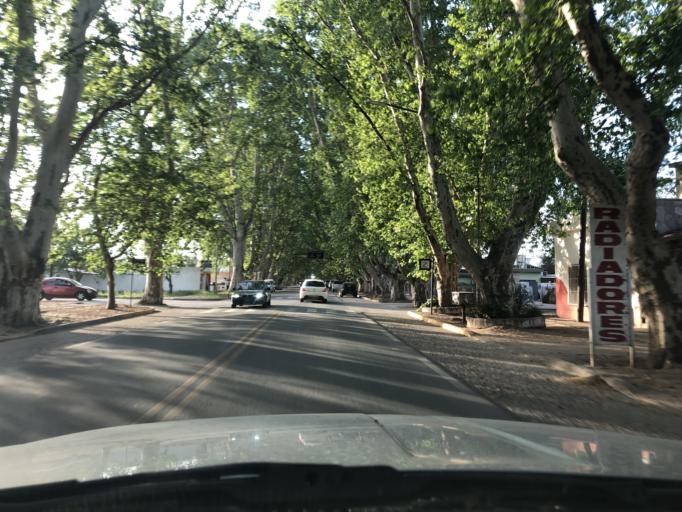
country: AR
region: Cordoba
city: Jesus Maria
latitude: -30.9938
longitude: -64.0940
